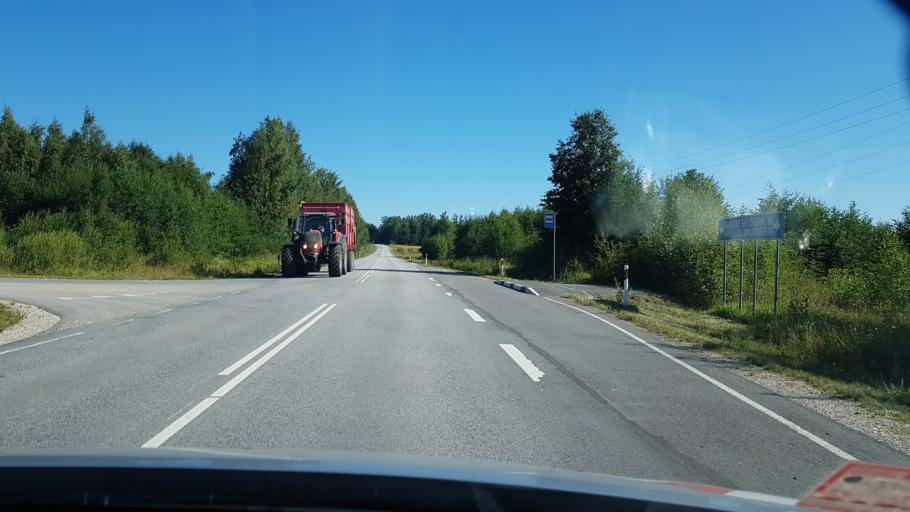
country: EE
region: Jogevamaa
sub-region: Mustvee linn
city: Mustvee
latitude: 58.9580
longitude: 26.8249
